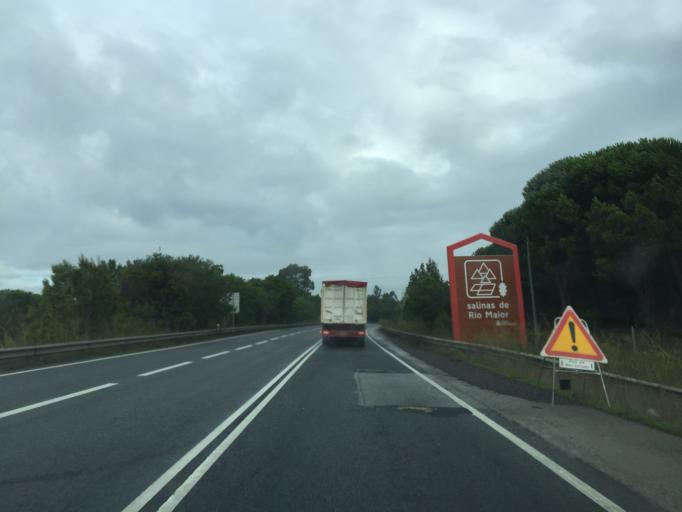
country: PT
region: Lisbon
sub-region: Azambuja
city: Alcoentre
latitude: 39.2562
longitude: -8.9521
